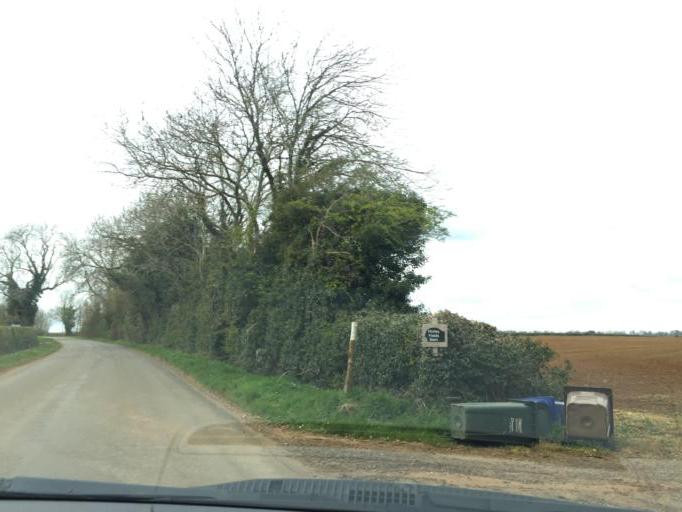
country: GB
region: England
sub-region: Oxfordshire
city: Hanwell
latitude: 52.1053
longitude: -1.4222
